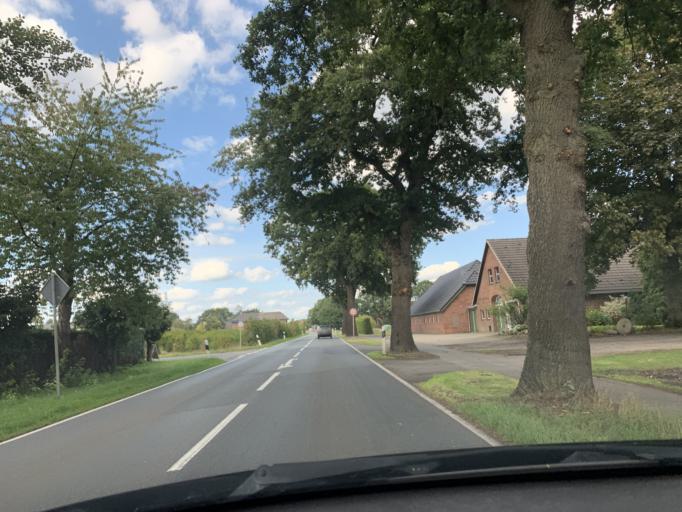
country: DE
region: Lower Saxony
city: Bad Zwischenahn
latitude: 53.1649
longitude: 7.9991
